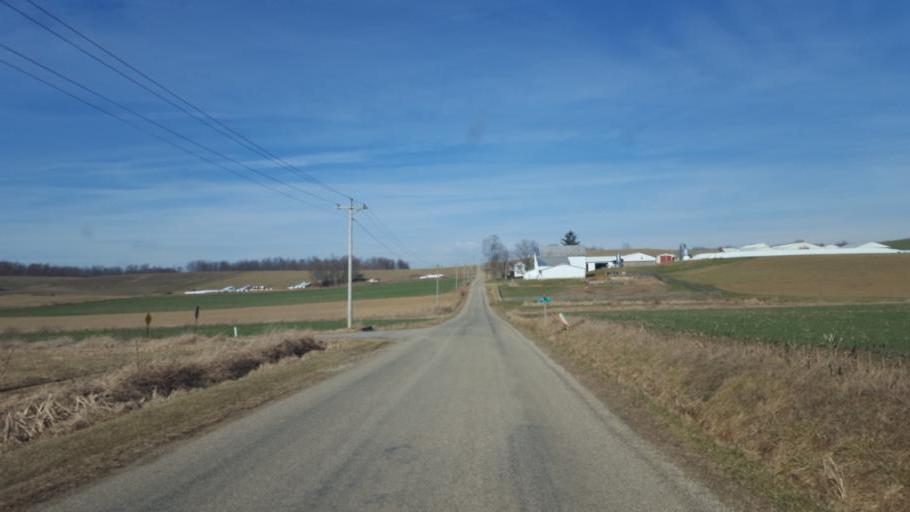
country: US
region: Ohio
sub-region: Knox County
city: Fredericktown
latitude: 40.5177
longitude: -82.4453
